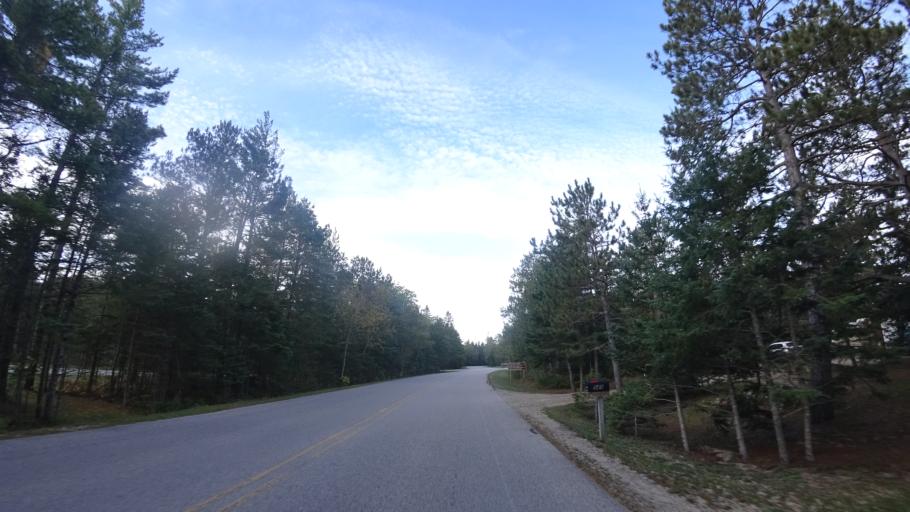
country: US
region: Michigan
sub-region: Mackinac County
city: Saint Ignace
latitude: 45.7475
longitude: -84.8935
